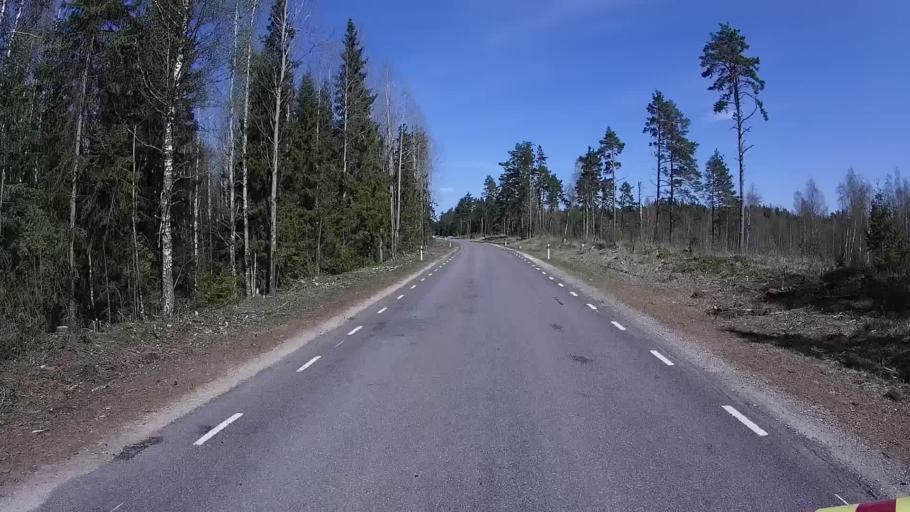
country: EE
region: Harju
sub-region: Nissi vald
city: Turba
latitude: 59.1175
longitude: 24.0577
